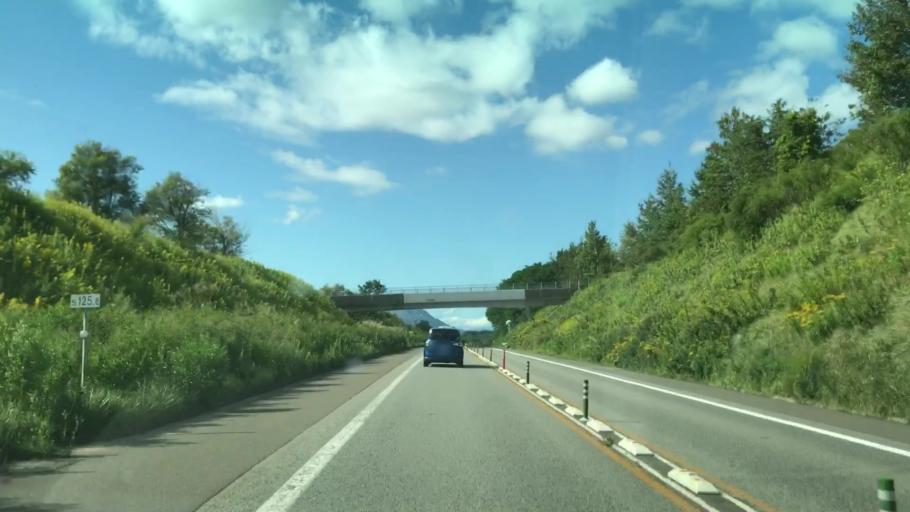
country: JP
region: Hokkaido
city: Date
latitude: 42.4233
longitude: 140.9294
